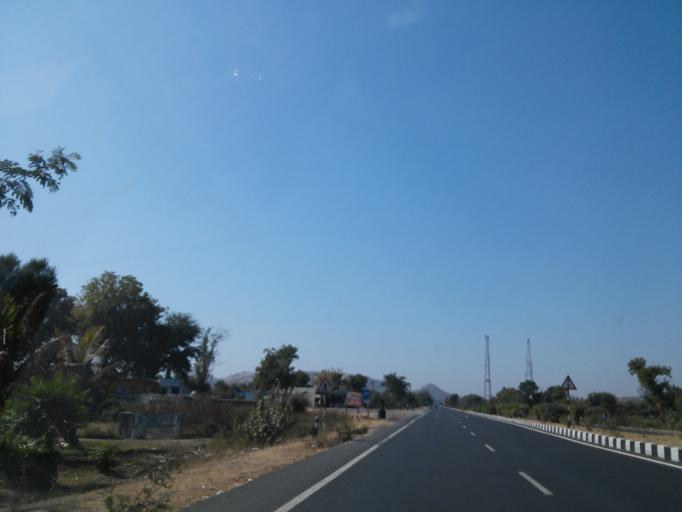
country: IN
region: Gujarat
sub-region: Sabar Kantha
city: Modasa
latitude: 23.6214
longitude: 73.2877
